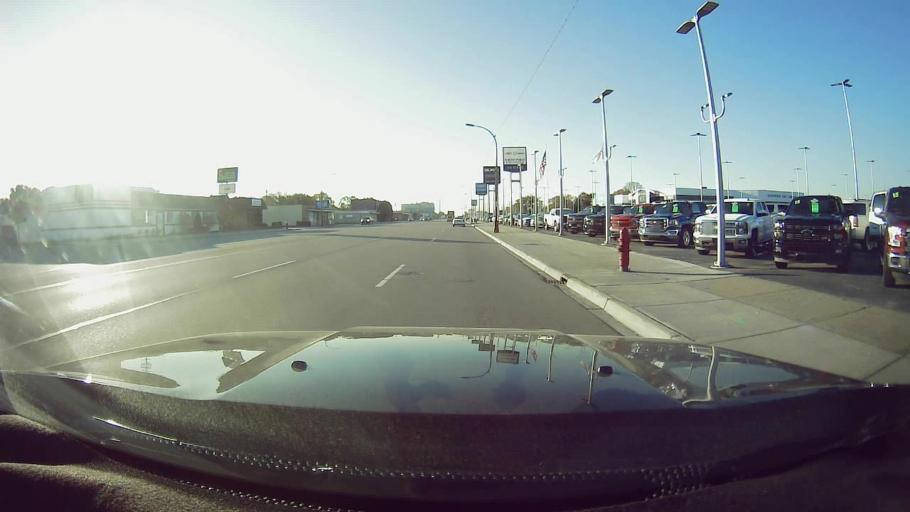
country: US
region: Michigan
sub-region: Macomb County
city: Center Line
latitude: 42.4872
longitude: -83.0277
